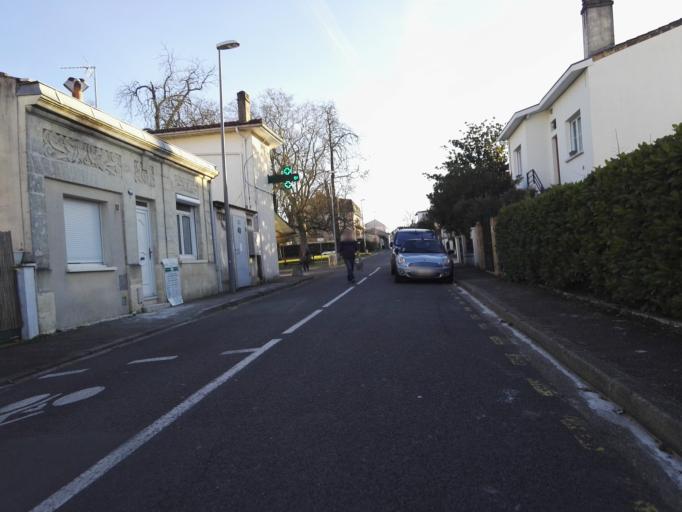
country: FR
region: Aquitaine
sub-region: Departement de la Gironde
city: Talence
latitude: 44.8085
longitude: -0.5852
